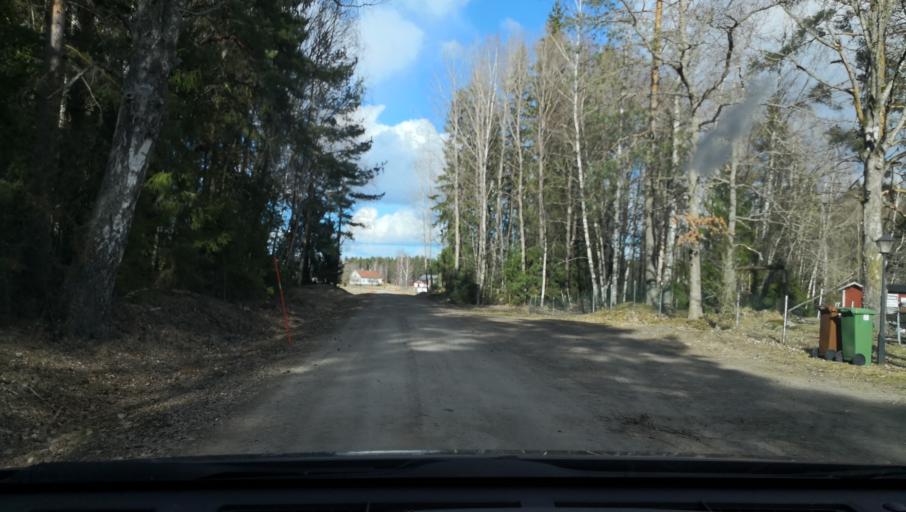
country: SE
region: OErebro
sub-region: Lindesbergs Kommun
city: Fellingsbro
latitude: 59.4315
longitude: 15.6864
